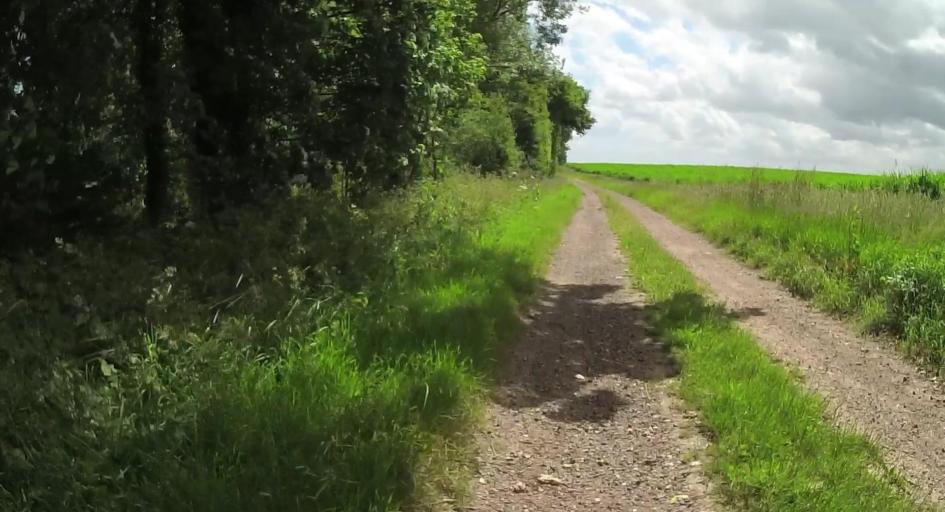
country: GB
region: England
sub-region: Hampshire
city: Basingstoke
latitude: 51.1827
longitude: -1.1642
